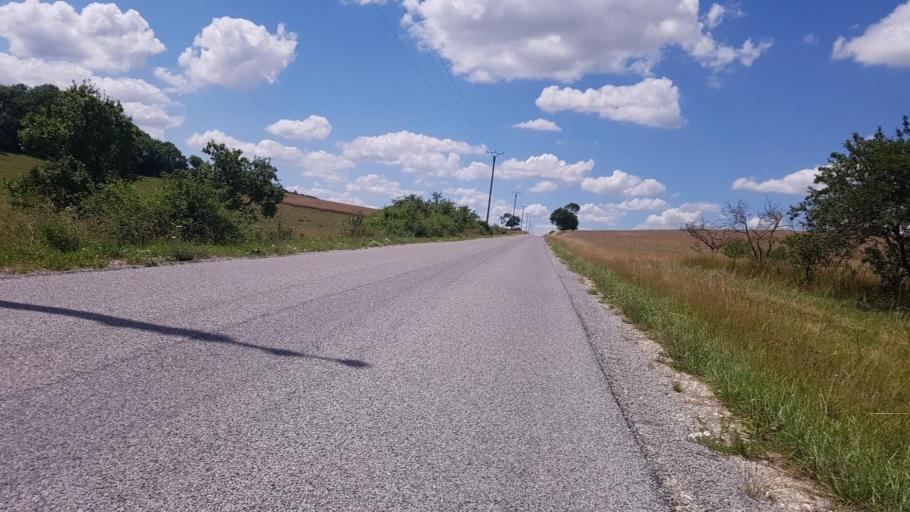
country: FR
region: Lorraine
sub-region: Departement de la Meuse
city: Vacon
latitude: 48.6586
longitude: 5.5437
